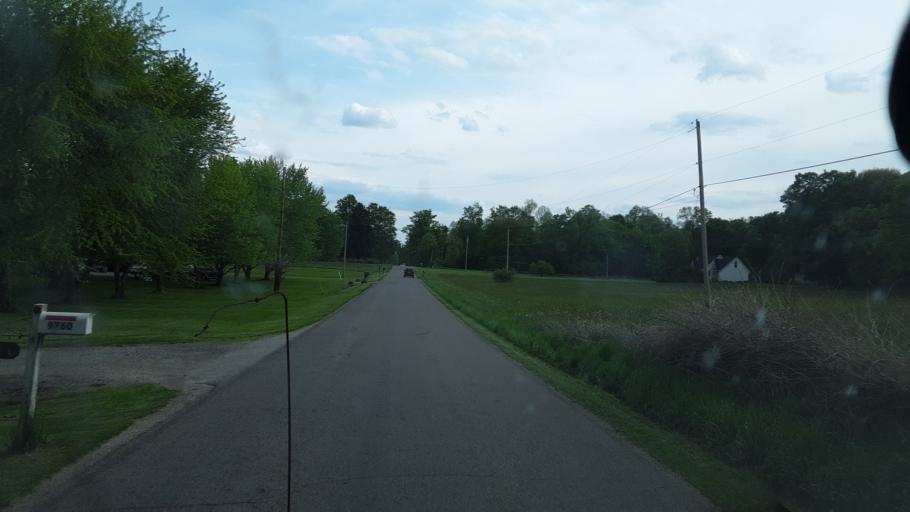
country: US
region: Ohio
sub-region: Portage County
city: Windham
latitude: 41.2578
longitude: -81.0667
